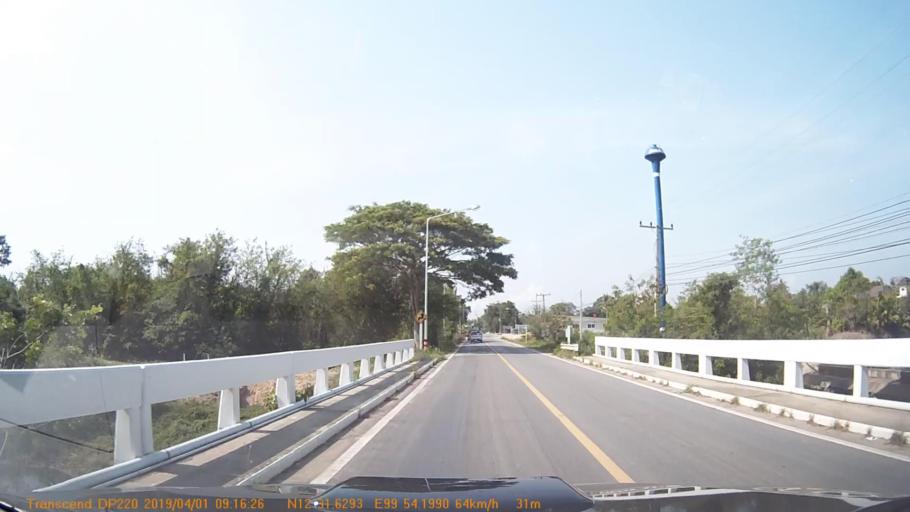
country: TH
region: Prachuap Khiri Khan
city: Hua Hin
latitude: 12.5269
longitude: 99.9032
